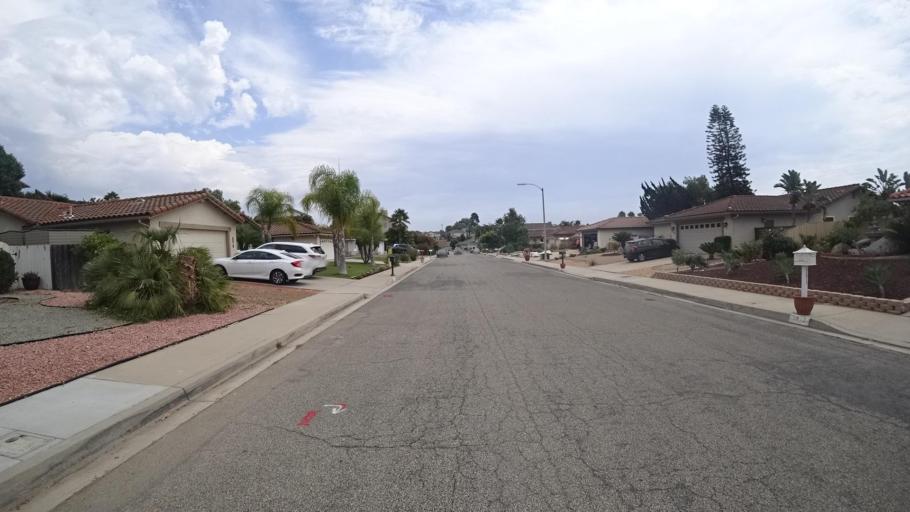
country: US
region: California
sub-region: San Diego County
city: Escondido
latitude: 33.1520
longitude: -117.1155
